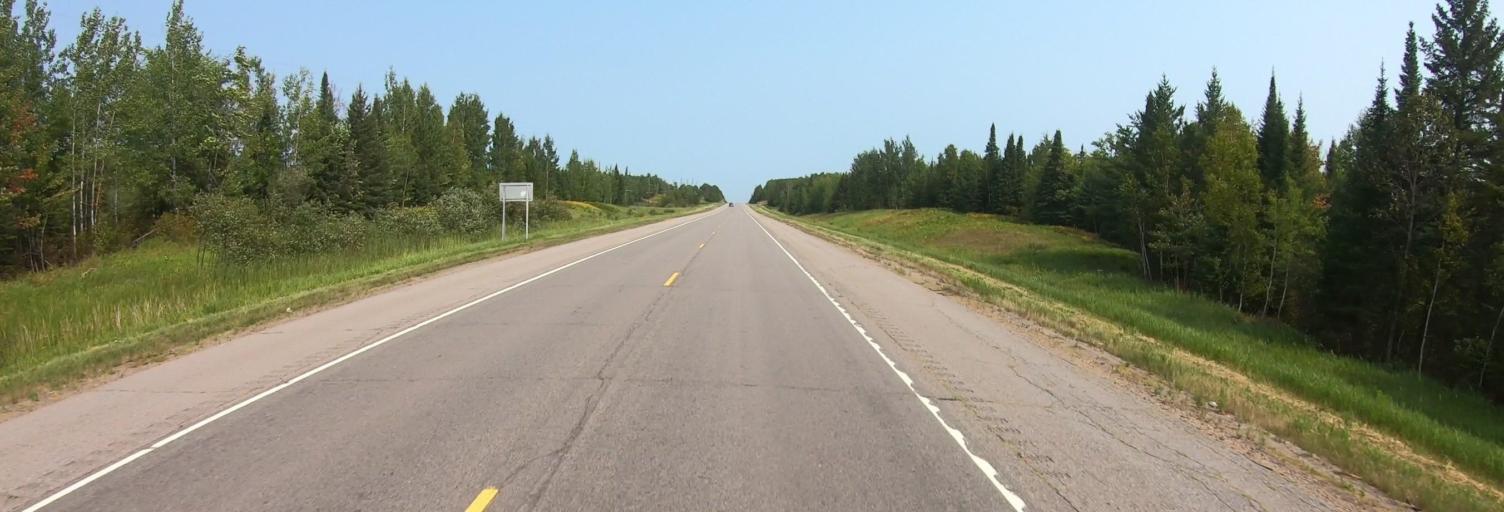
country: US
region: Minnesota
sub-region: Saint Louis County
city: Mountain Iron
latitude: 47.9936
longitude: -92.8309
